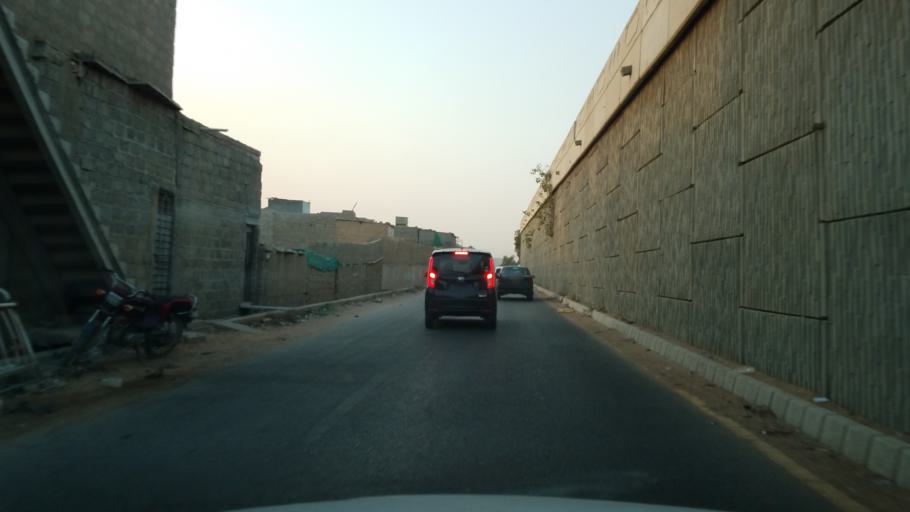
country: PK
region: Sindh
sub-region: Karachi District
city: Karachi
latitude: 24.9434
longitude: 67.0876
